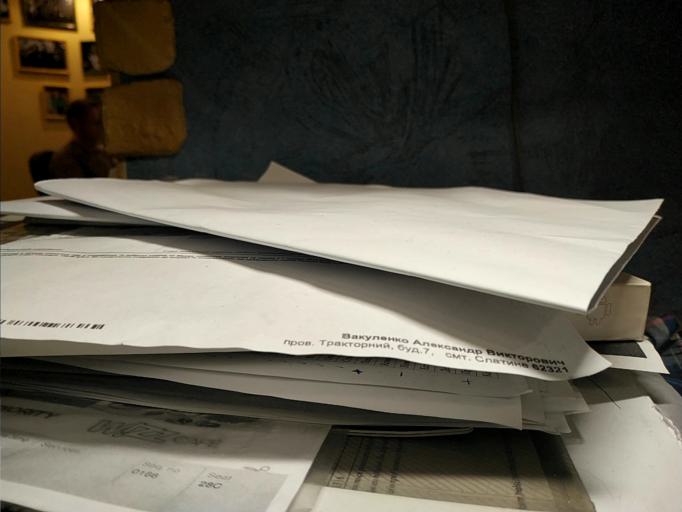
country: RU
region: Tverskaya
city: Zubtsov
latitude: 56.1196
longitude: 34.5764
